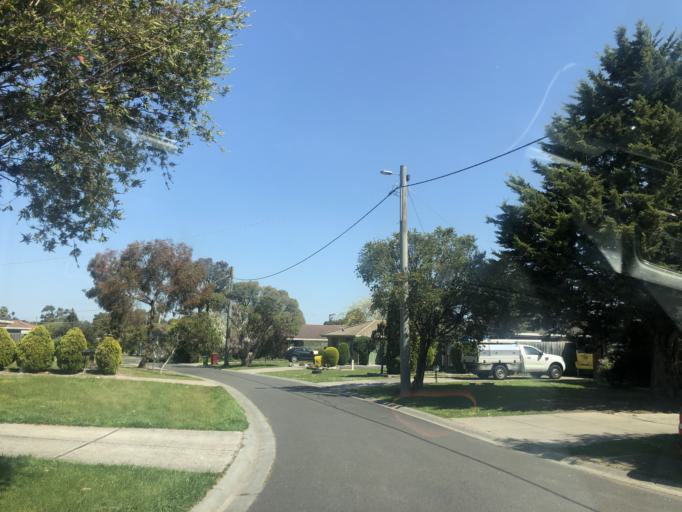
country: AU
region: Victoria
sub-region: Casey
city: Narre Warren South
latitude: -38.0325
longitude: 145.2817
